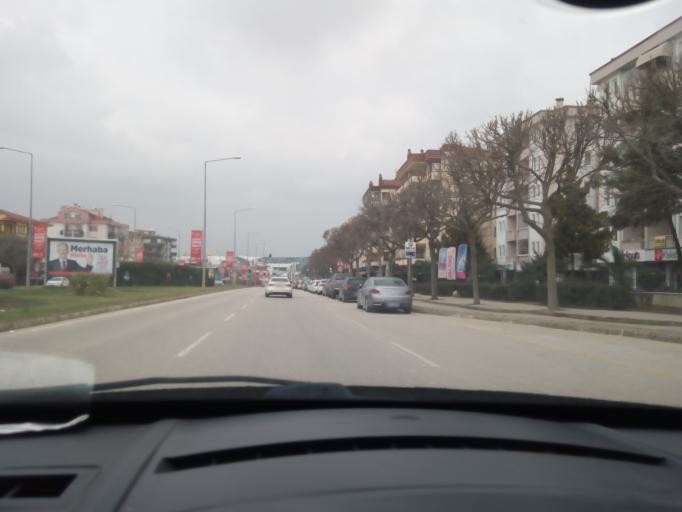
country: TR
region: Bursa
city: Yildirim
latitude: 40.2255
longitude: 28.9795
